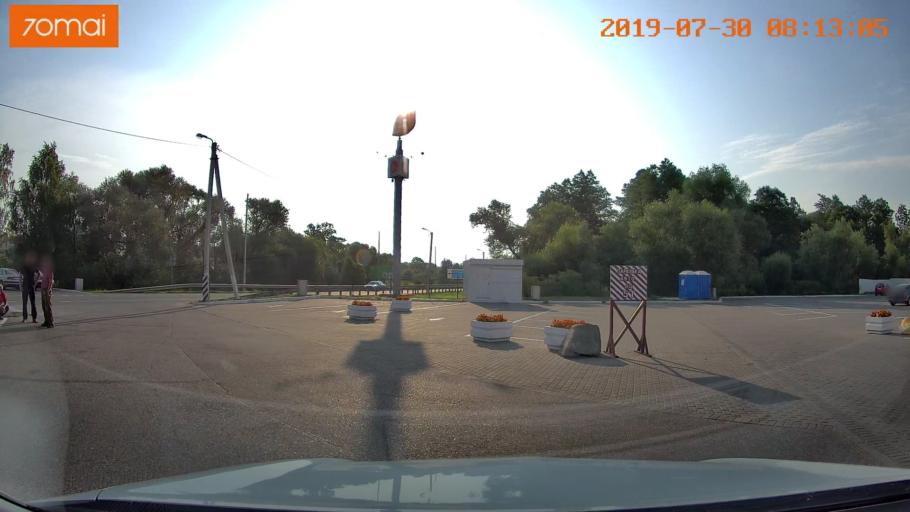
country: RU
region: Kaliningrad
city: Gvardeysk
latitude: 54.6504
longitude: 21.3421
